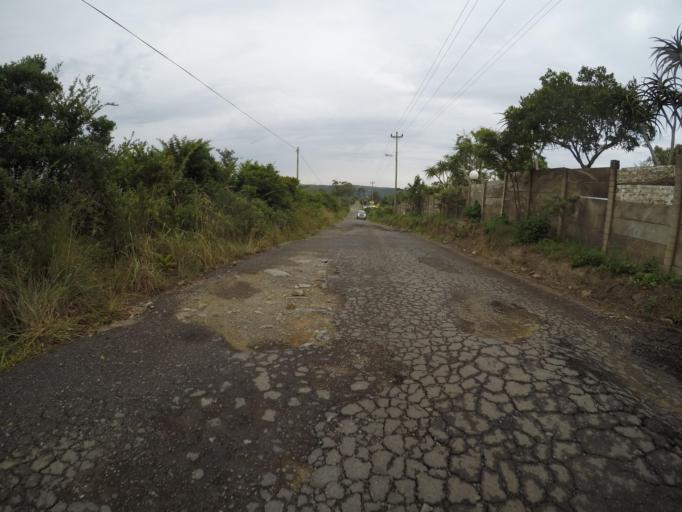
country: ZA
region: Eastern Cape
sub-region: Buffalo City Metropolitan Municipality
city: East London
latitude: -32.9608
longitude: 27.8414
